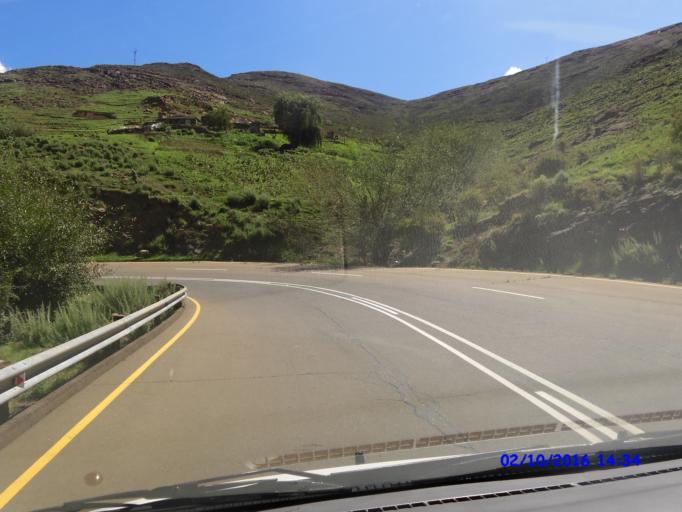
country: LS
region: Maseru
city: Nako
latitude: -29.4904
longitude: 28.0573
